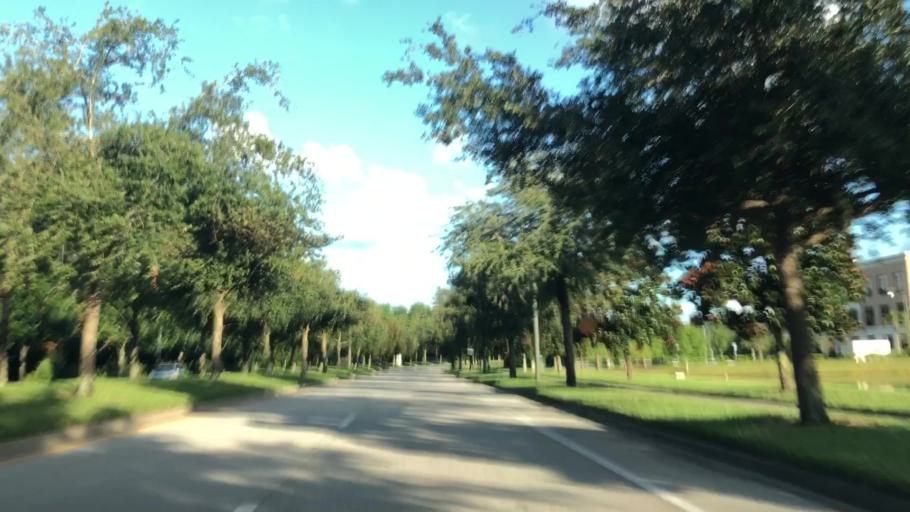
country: US
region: Florida
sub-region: Saint Johns County
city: Palm Valley
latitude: 30.1221
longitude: -81.4201
